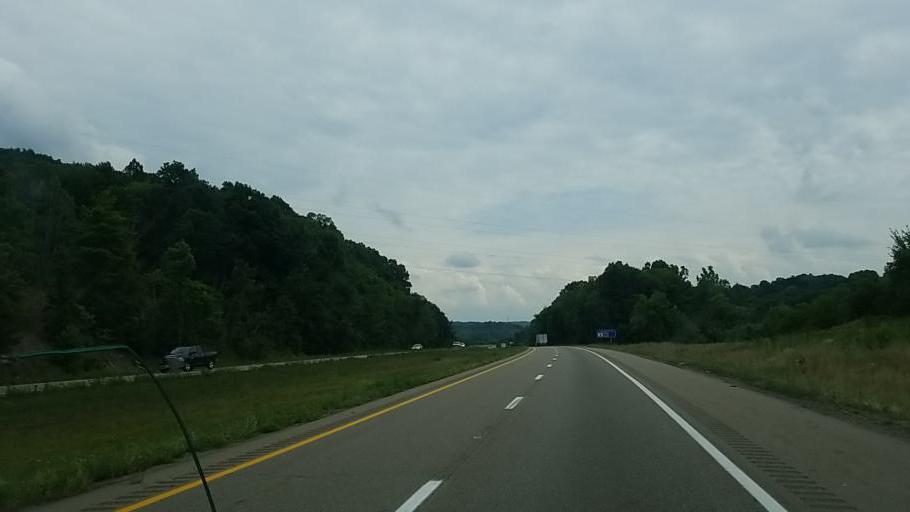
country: US
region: Ohio
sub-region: Tuscarawas County
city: Newcomerstown
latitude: 40.3065
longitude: -81.5668
